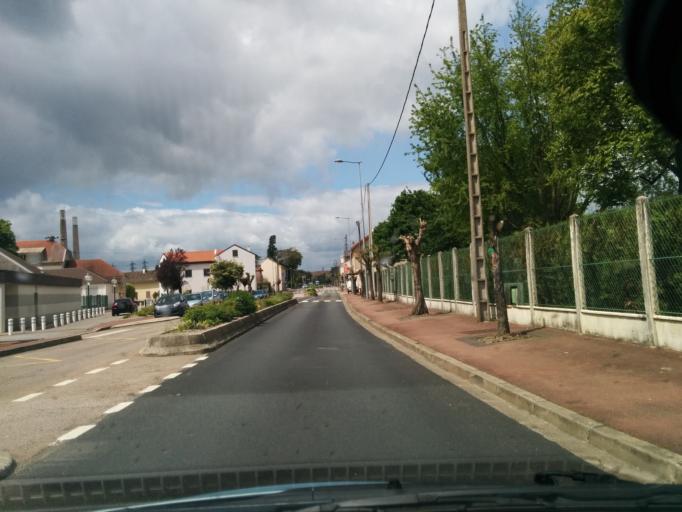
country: FR
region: Ile-de-France
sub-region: Departement des Yvelines
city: Porcheville
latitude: 48.9715
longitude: 1.7811
